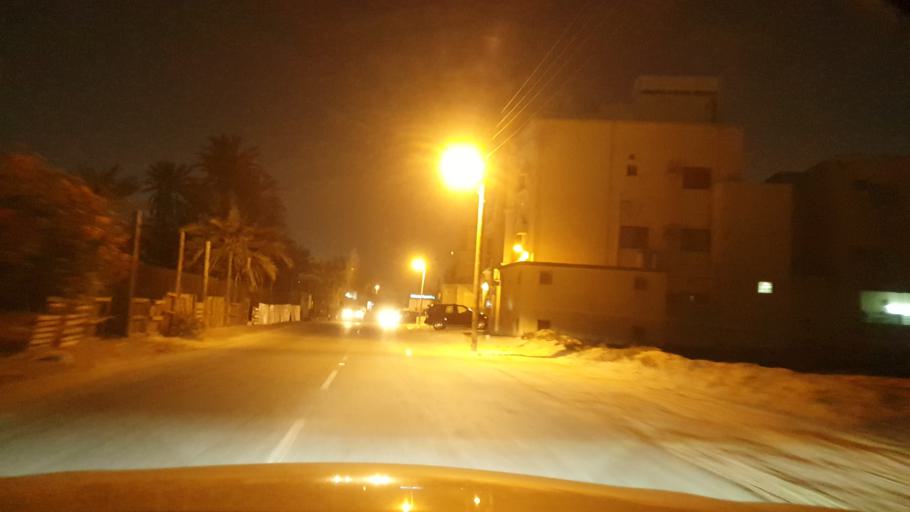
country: BH
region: Manama
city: Jidd Hafs
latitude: 26.2035
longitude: 50.5421
